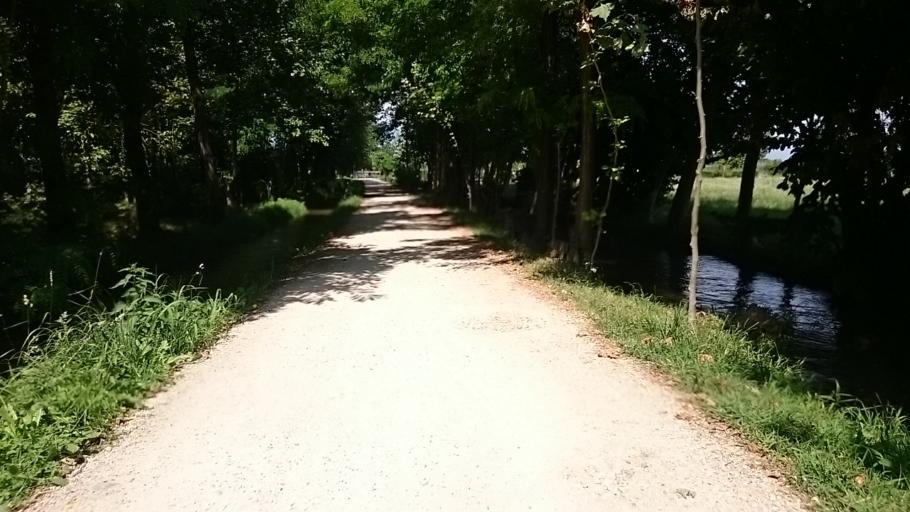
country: IT
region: Veneto
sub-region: Provincia di Vicenza
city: Rosa
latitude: 45.7083
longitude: 11.7374
